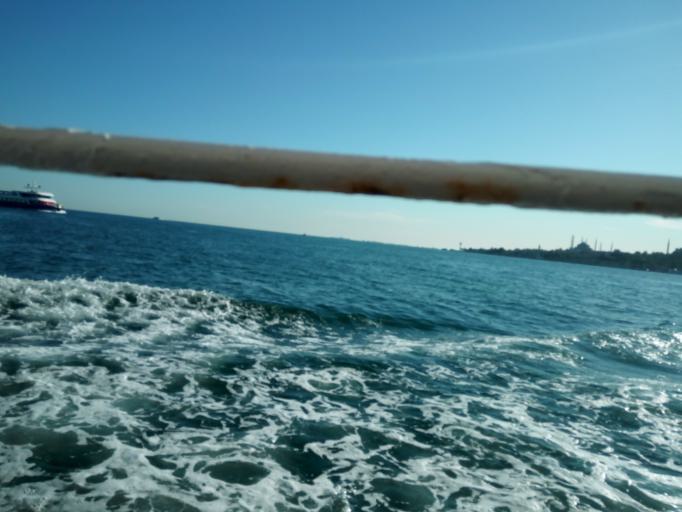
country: TR
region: Istanbul
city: UEskuedar
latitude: 41.0109
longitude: 29.0013
